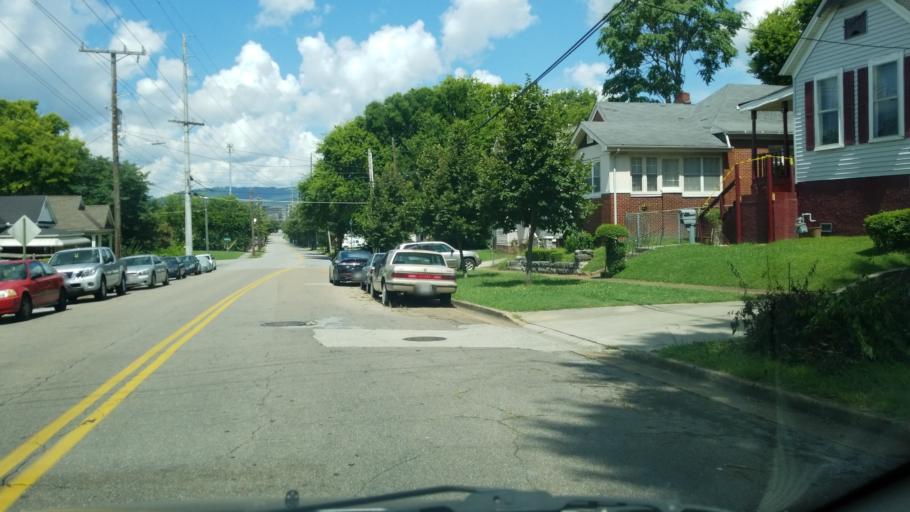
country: US
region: Tennessee
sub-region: Hamilton County
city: Chattanooga
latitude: 35.0399
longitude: -85.2961
